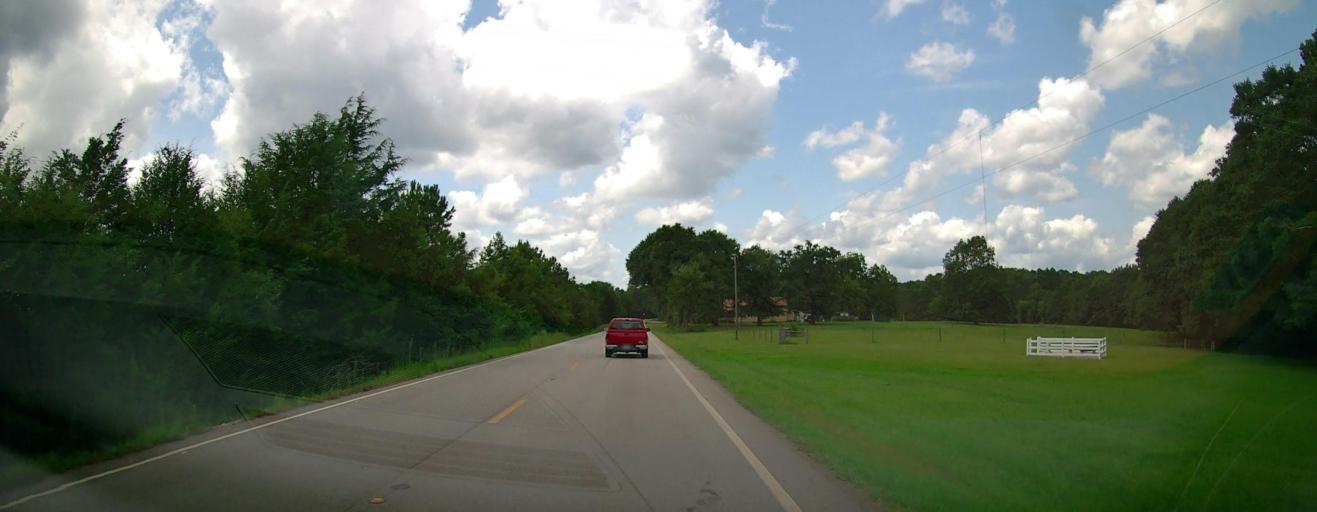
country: US
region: Georgia
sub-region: Meriwether County
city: Greenville
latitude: 33.0671
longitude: -84.7663
